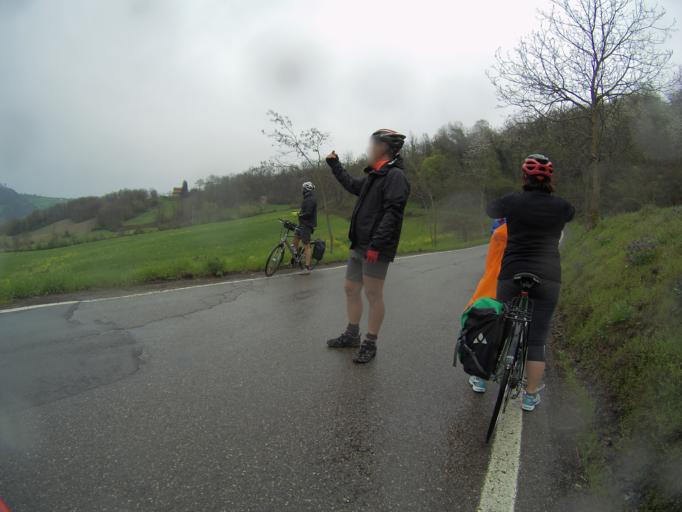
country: IT
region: Emilia-Romagna
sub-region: Provincia di Reggio Emilia
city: Ciano d'Enza
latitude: 44.5675
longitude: 10.4107
